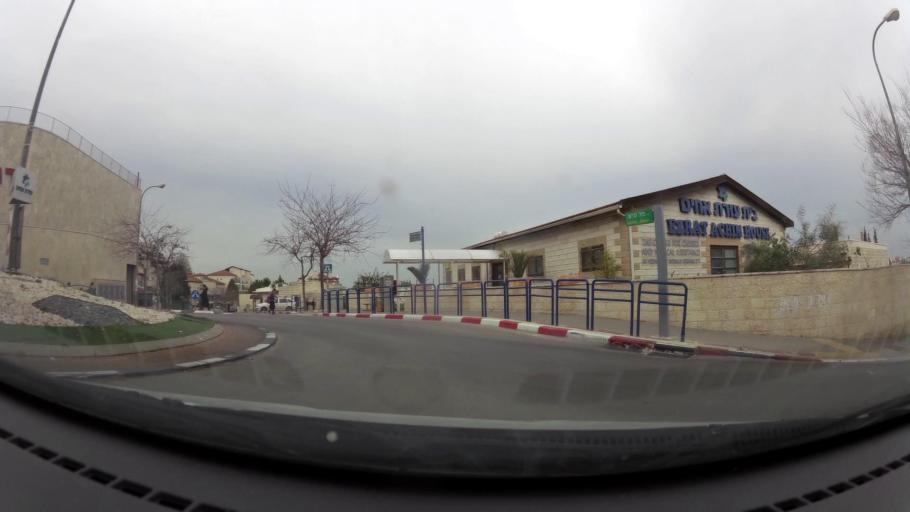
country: IL
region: Jerusalem
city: Bet Shemesh
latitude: 31.7136
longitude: 34.9957
